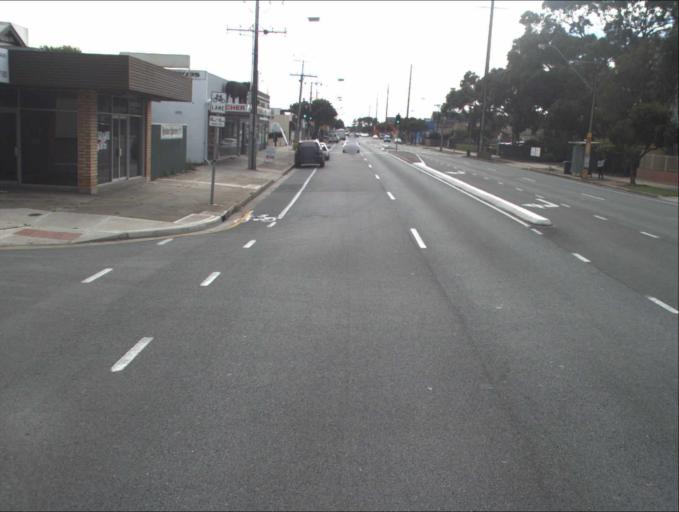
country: AU
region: South Australia
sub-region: Charles Sturt
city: Royal Park
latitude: -34.8740
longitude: 138.5124
